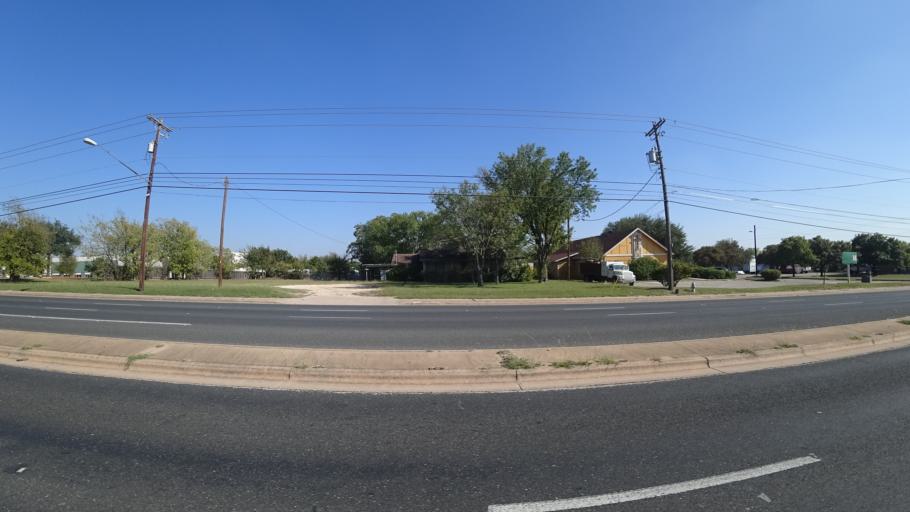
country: US
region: Texas
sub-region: Travis County
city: Wells Branch
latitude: 30.3531
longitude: -97.6747
